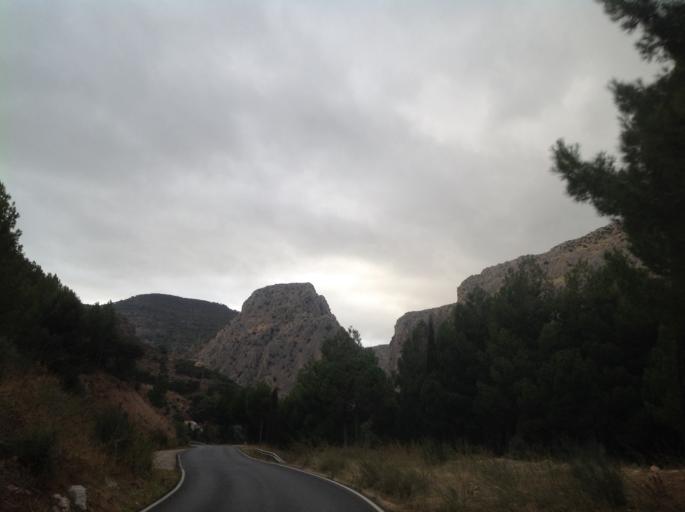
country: ES
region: Andalusia
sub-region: Provincia de Malaga
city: Carratraca
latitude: 36.9097
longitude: -4.7643
